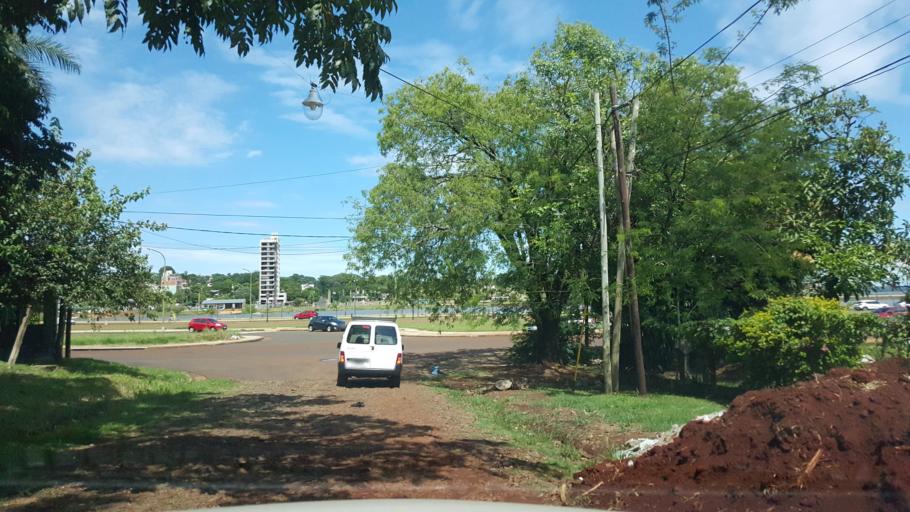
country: AR
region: Misiones
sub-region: Departamento de Capital
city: Posadas
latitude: -27.3580
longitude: -55.9072
